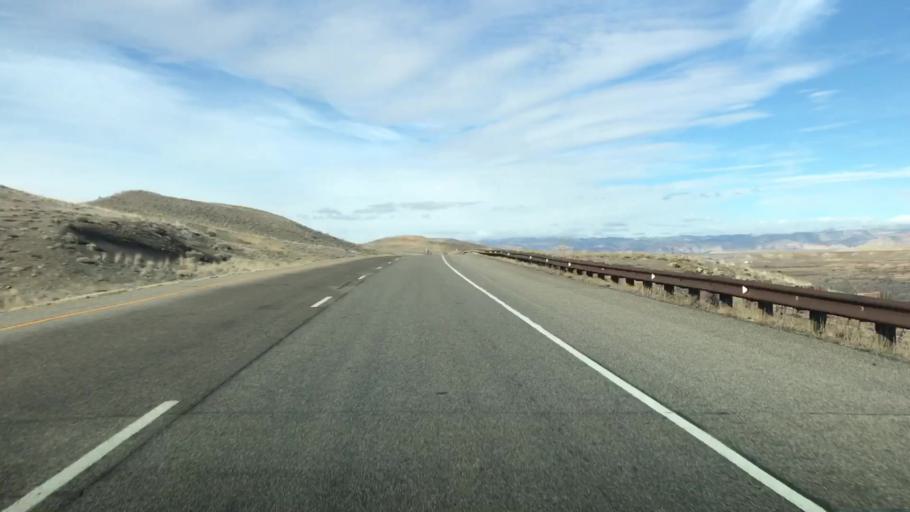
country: US
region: Colorado
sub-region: Mesa County
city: Loma
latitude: 39.2264
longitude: -108.8972
